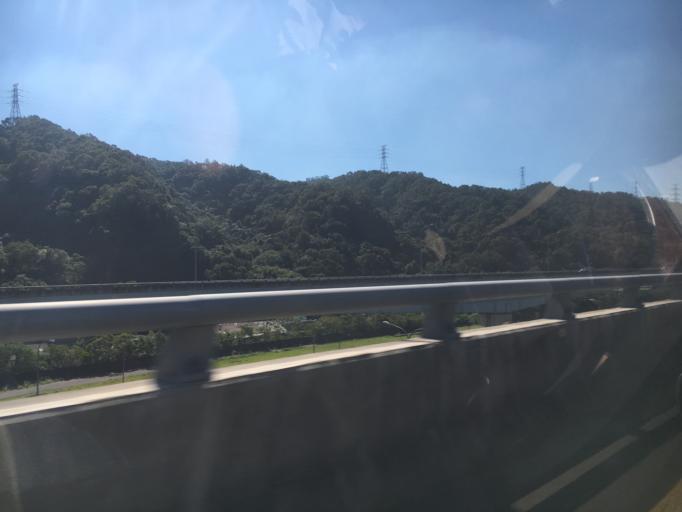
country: TW
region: Taipei
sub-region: Taipei
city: Banqiao
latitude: 25.0629
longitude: 121.4171
